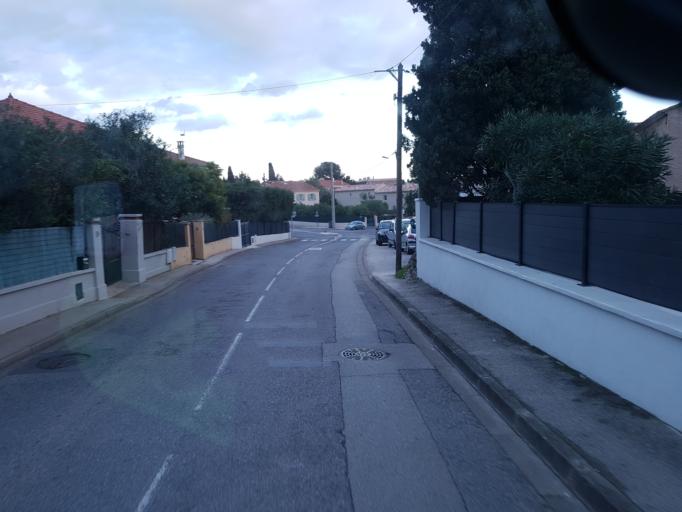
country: FR
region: Provence-Alpes-Cote d'Azur
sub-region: Departement du Var
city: Bandol
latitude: 43.1398
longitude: 5.7417
